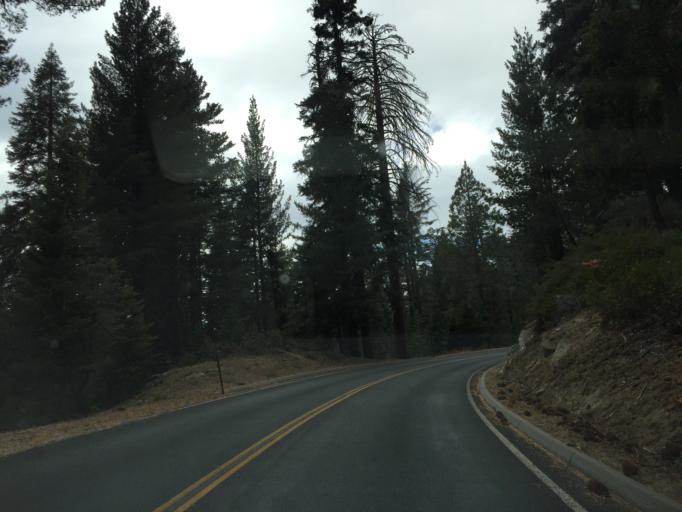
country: US
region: California
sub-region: Fresno County
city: Squaw Valley
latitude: 36.7327
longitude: -118.9620
